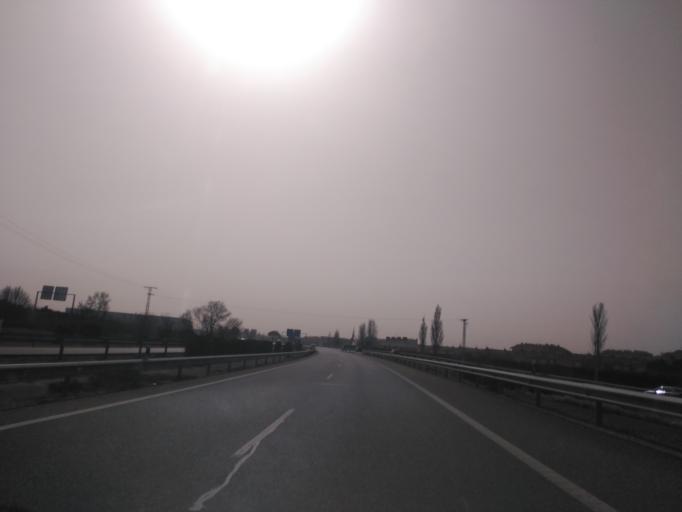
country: ES
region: Castille and Leon
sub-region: Provincia de Palencia
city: Villamuriel de Cerrato
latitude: 41.9501
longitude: -4.5046
